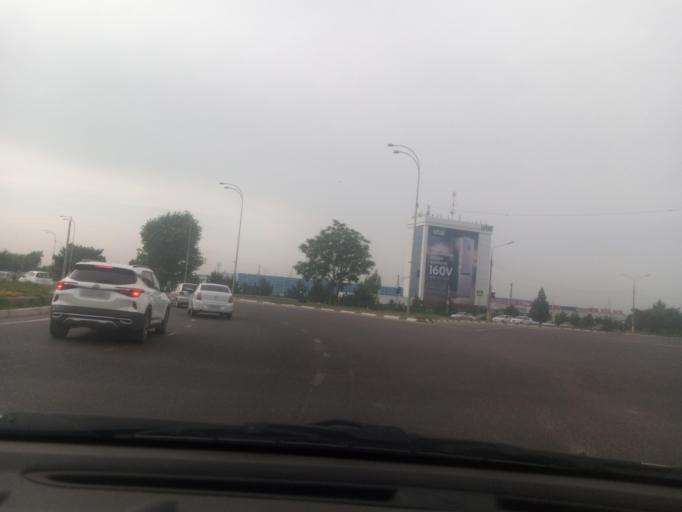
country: UZ
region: Toshkent Shahri
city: Bektemir
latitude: 41.2677
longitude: 69.3662
